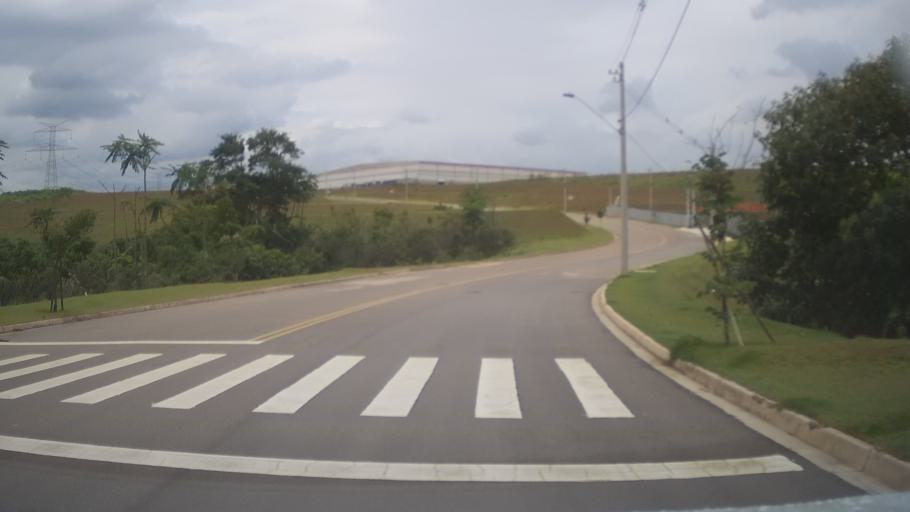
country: BR
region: Sao Paulo
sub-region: Itupeva
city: Itupeva
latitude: -23.1675
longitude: -47.0013
